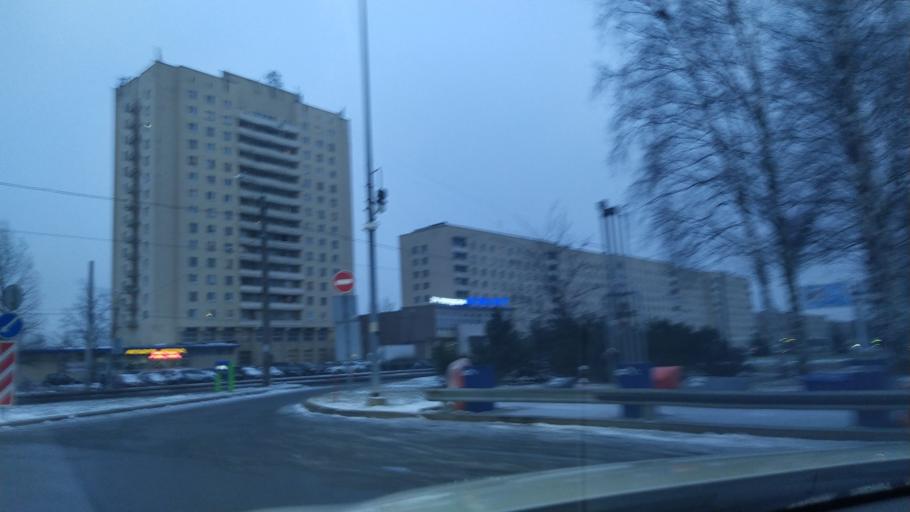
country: RU
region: St.-Petersburg
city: Grazhdanka
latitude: 60.0147
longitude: 30.4328
